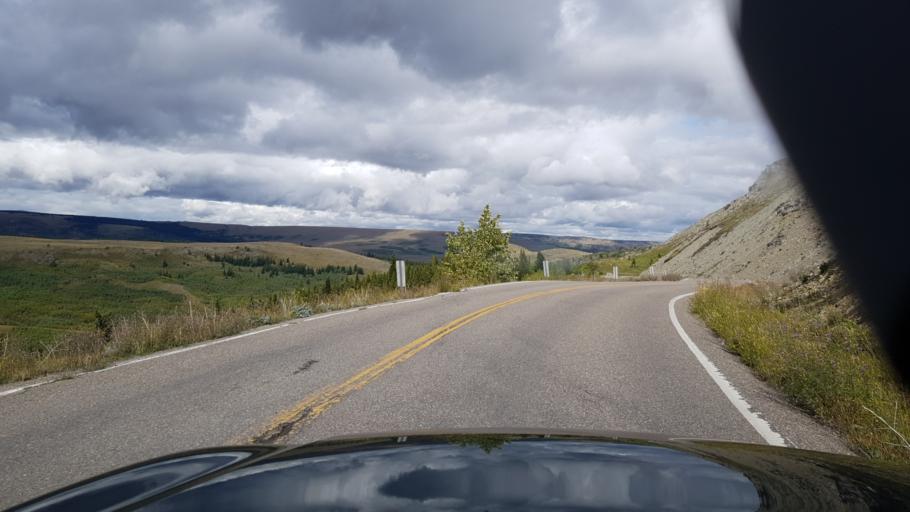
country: US
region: Montana
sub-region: Glacier County
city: South Browning
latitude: 48.5382
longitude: -113.3062
